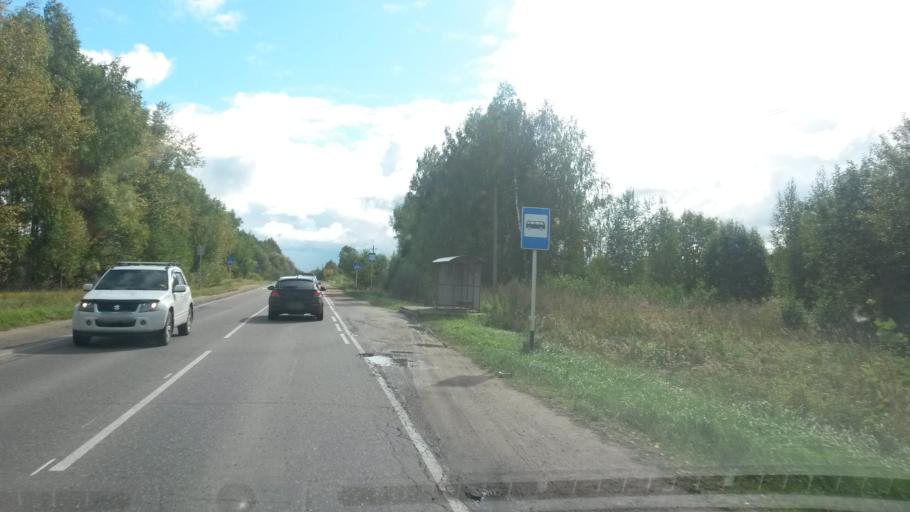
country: RU
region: Ivanovo
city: Zavolzhsk
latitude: 57.5054
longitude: 42.1008
